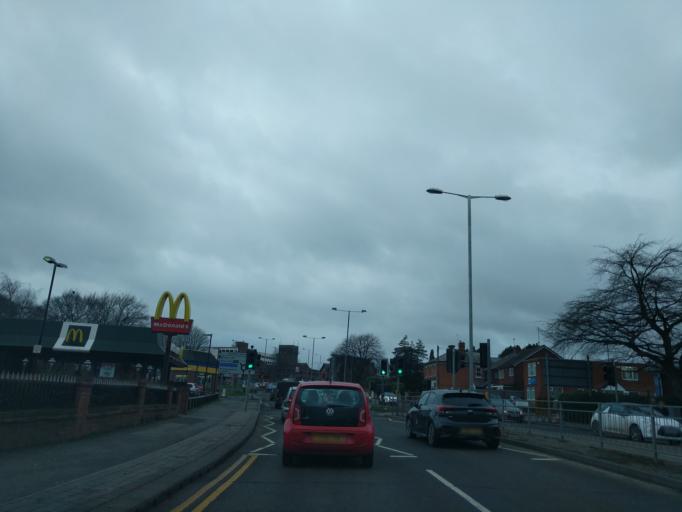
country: GB
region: England
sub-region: Staffordshire
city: Cannock
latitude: 52.6898
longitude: -2.0251
